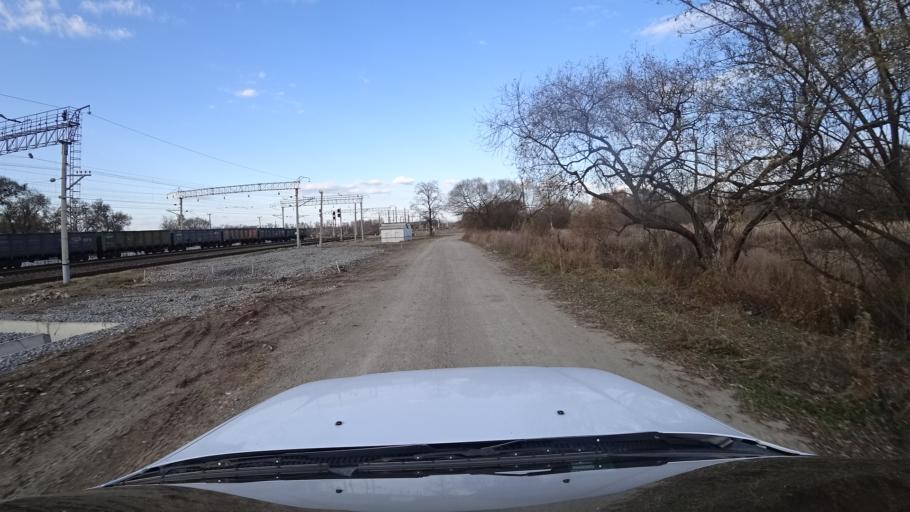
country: RU
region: Primorskiy
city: Lazo
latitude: 45.8225
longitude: 133.6135
